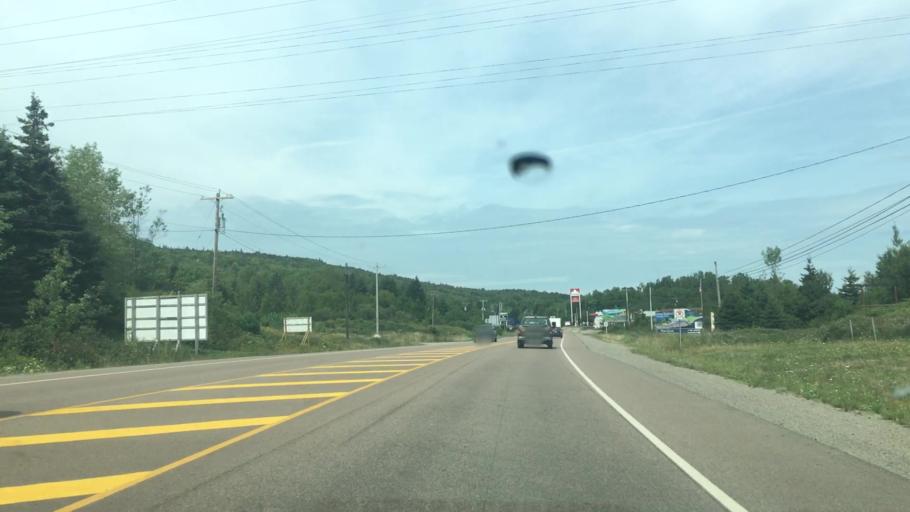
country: CA
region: Nova Scotia
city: Port Hawkesbury
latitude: 45.6501
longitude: -61.4415
